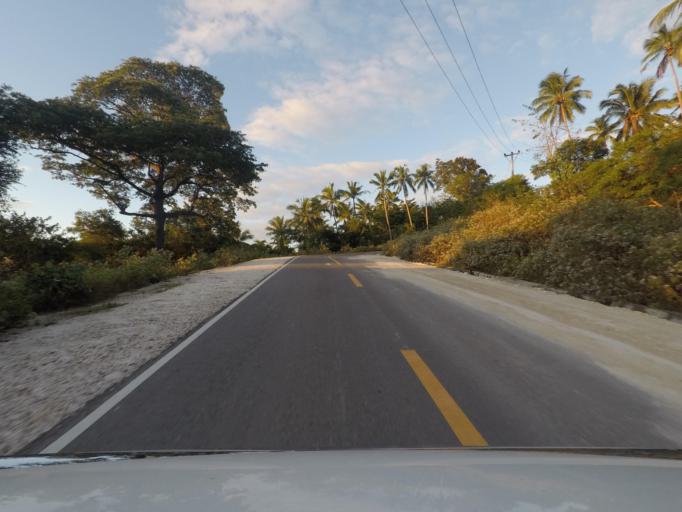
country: TL
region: Lautem
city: Lospalos
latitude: -8.3981
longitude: 127.2716
